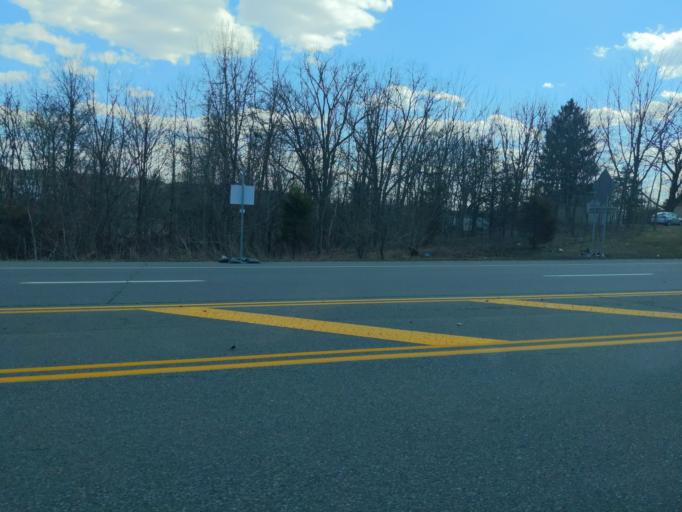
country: US
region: Pennsylvania
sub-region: Montgomery County
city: East Greenville
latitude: 40.4025
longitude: -75.4929
